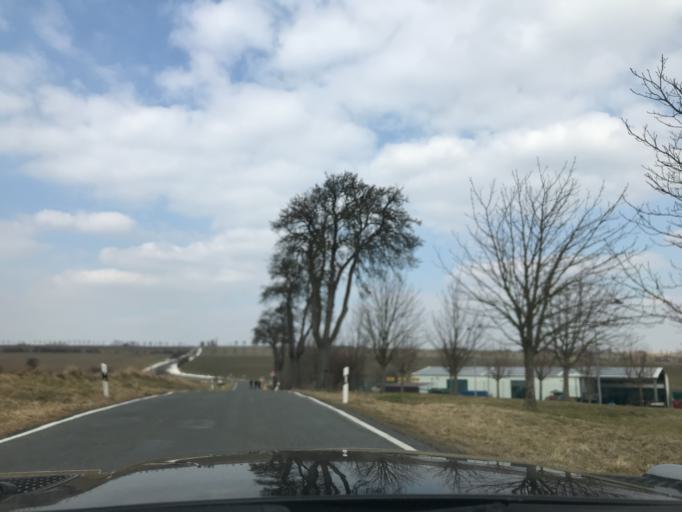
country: DE
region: Thuringia
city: Helmsdorf
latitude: 51.2595
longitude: 10.3975
